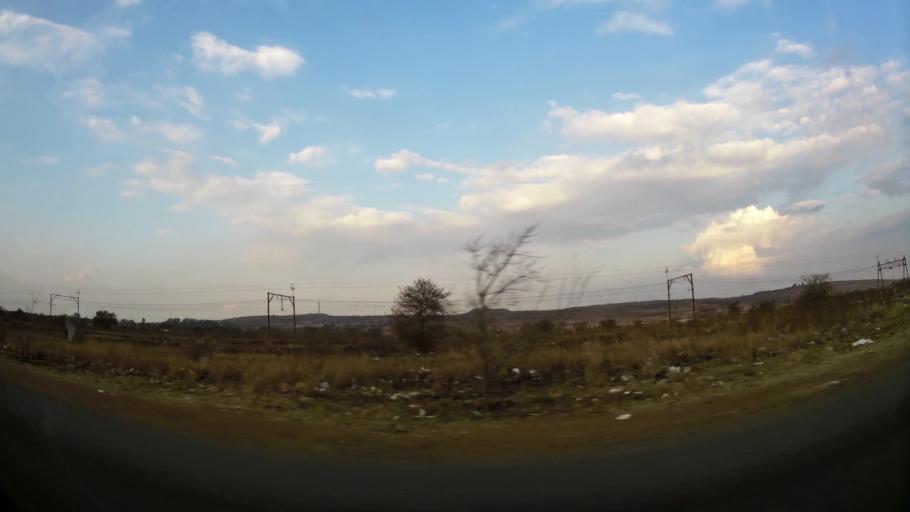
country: ZA
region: Gauteng
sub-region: City of Johannesburg Metropolitan Municipality
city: Orange Farm
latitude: -26.5823
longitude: 27.8554
